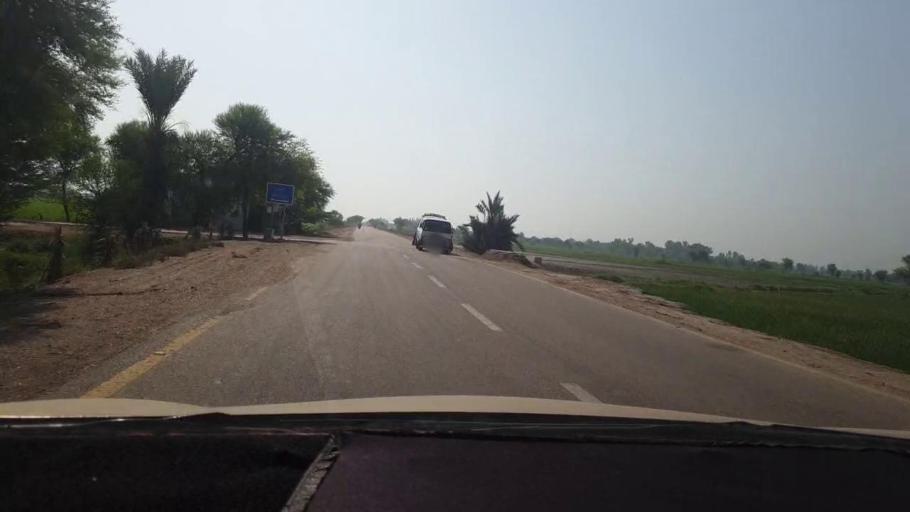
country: PK
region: Sindh
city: Miro Khan
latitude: 27.7286
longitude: 68.1324
